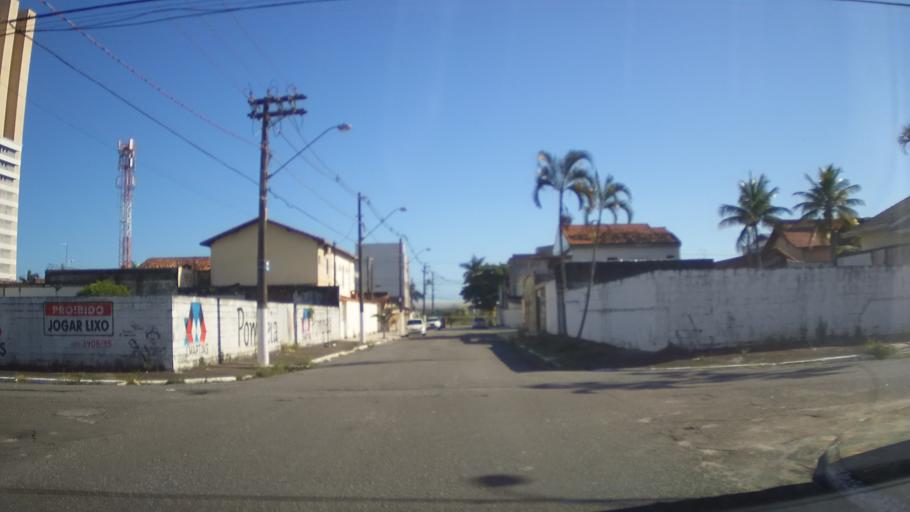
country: BR
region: Sao Paulo
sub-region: Praia Grande
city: Praia Grande
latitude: -24.0311
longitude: -46.4879
